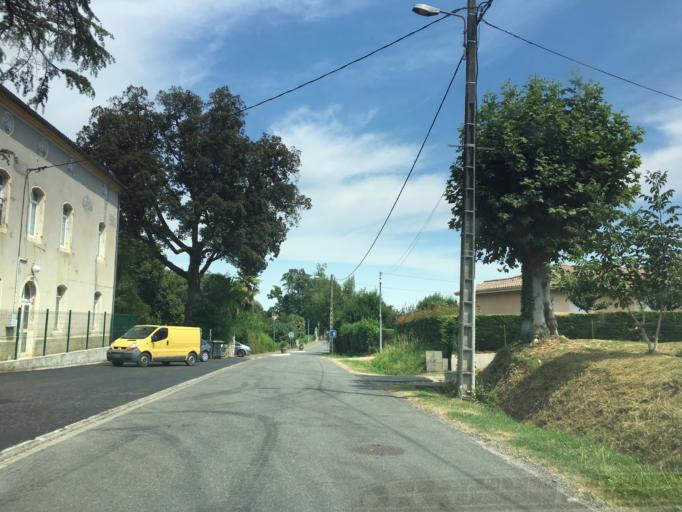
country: FR
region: Midi-Pyrenees
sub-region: Departement du Gers
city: Fleurance
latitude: 43.8437
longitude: 0.6577
